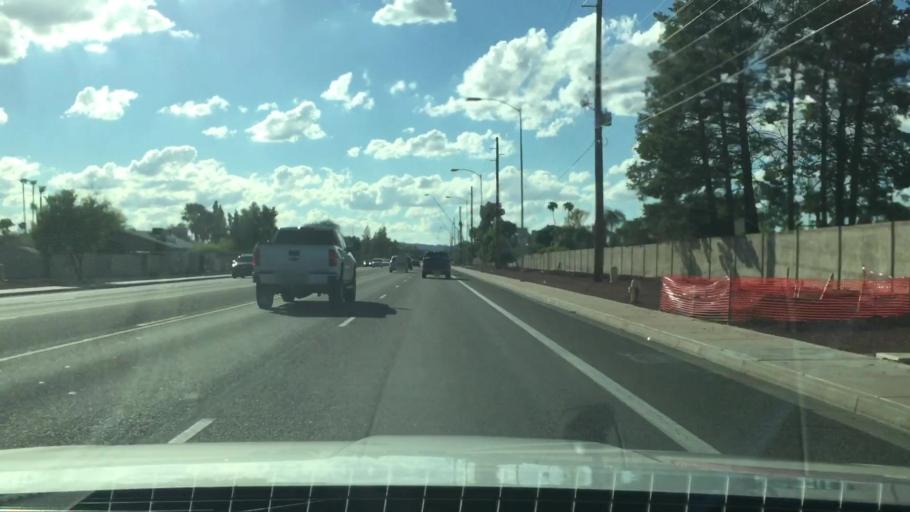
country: US
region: Arizona
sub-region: Maricopa County
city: San Carlos
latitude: 33.3640
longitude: -111.8871
